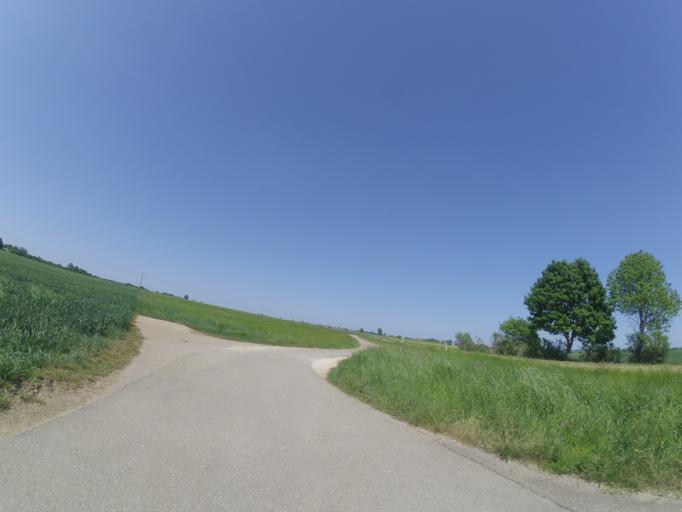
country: DE
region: Baden-Wuerttemberg
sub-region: Tuebingen Region
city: Nellingen
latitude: 48.5292
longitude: 9.7757
